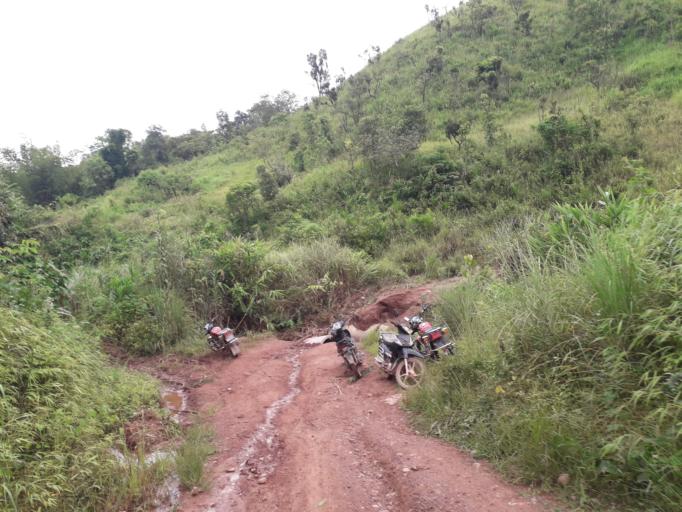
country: CN
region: Yunnan
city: Menglie
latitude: 22.2585
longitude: 101.5955
